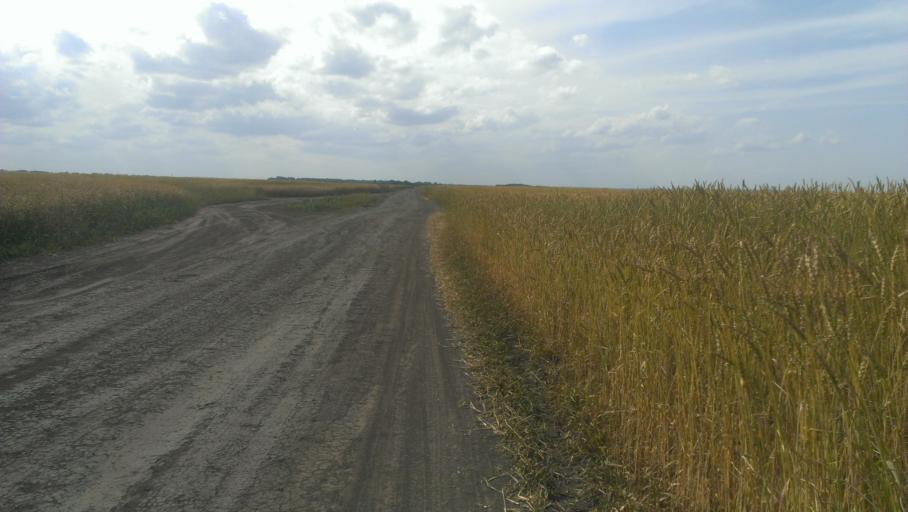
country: RU
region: Altai Krai
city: Gon'ba
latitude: 53.3753
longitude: 83.5552
